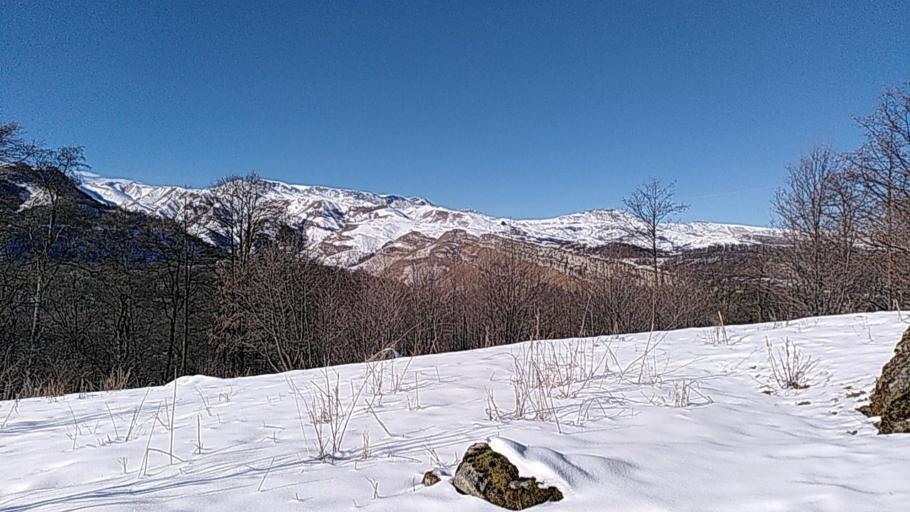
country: RU
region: Kabardino-Balkariya
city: Belaya Rechka
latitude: 43.3575
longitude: 43.4027
